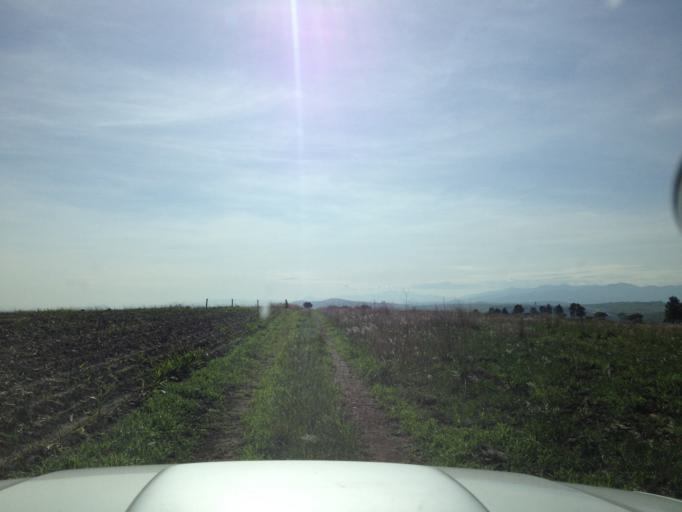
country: MX
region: Michoacan
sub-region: Tarimbaro
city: El Colegio
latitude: 19.7690
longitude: -101.1823
